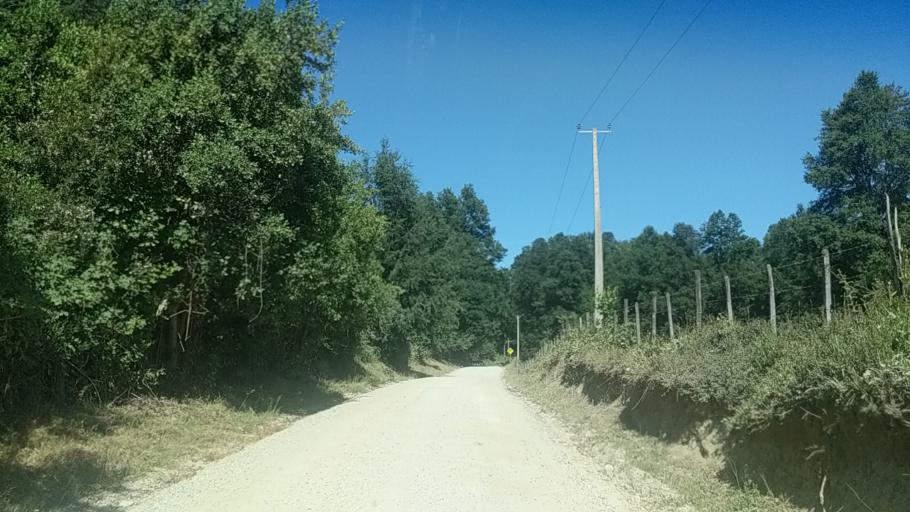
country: CL
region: Araucania
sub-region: Provincia de Cautin
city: Pucon
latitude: -39.0647
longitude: -71.7356
